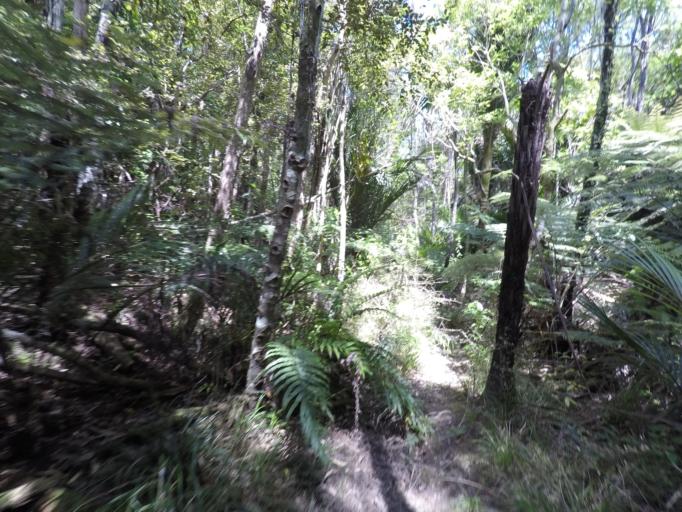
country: NZ
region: Auckland
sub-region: Auckland
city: Titirangi
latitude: -36.9737
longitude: 174.6309
